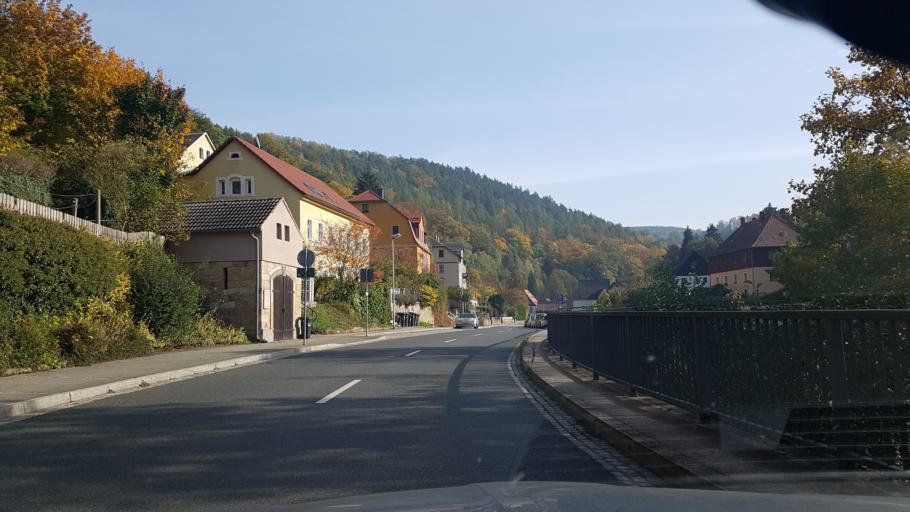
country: DE
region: Saxony
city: Konigstein
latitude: 50.9145
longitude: 14.0589
